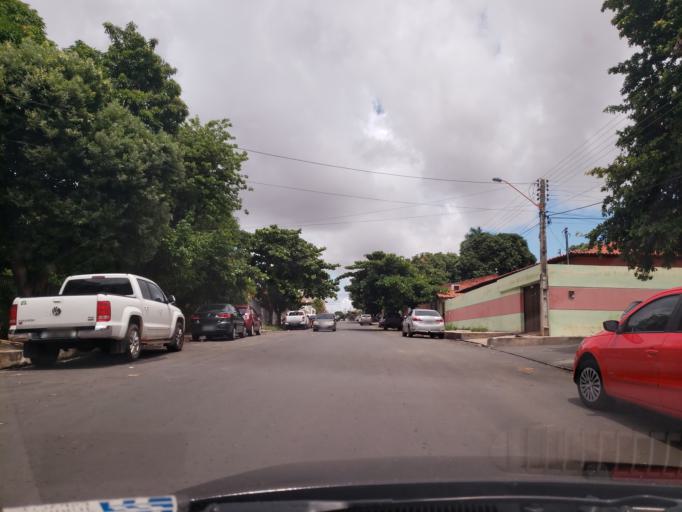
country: BR
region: Piaui
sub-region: Teresina
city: Teresina
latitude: -5.1094
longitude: -42.8114
